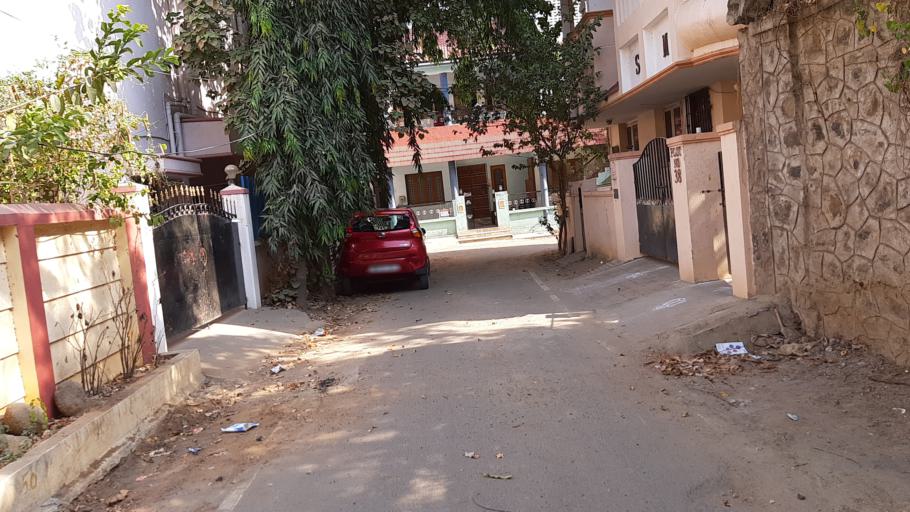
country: IN
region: Tamil Nadu
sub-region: Kancheepuram
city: Perungudi
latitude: 12.9815
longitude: 80.2290
